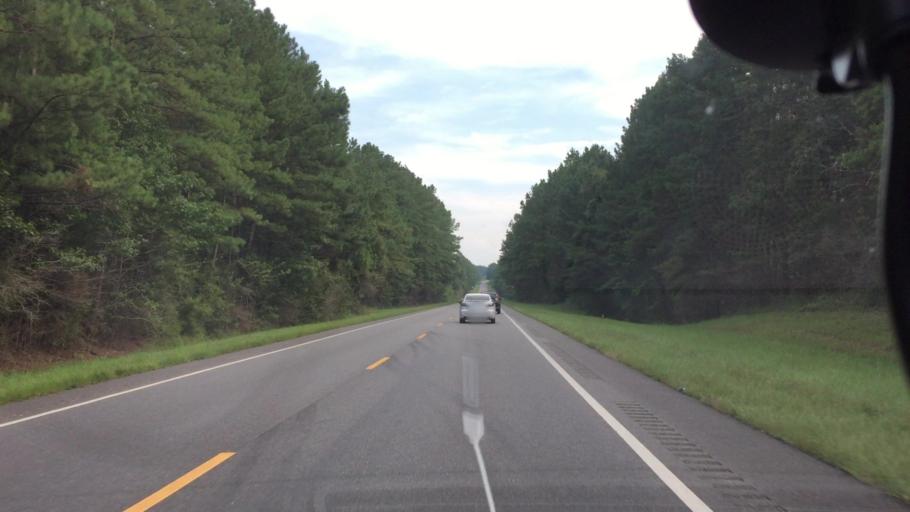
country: US
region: Alabama
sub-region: Coffee County
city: New Brockton
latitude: 31.5705
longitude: -85.9279
